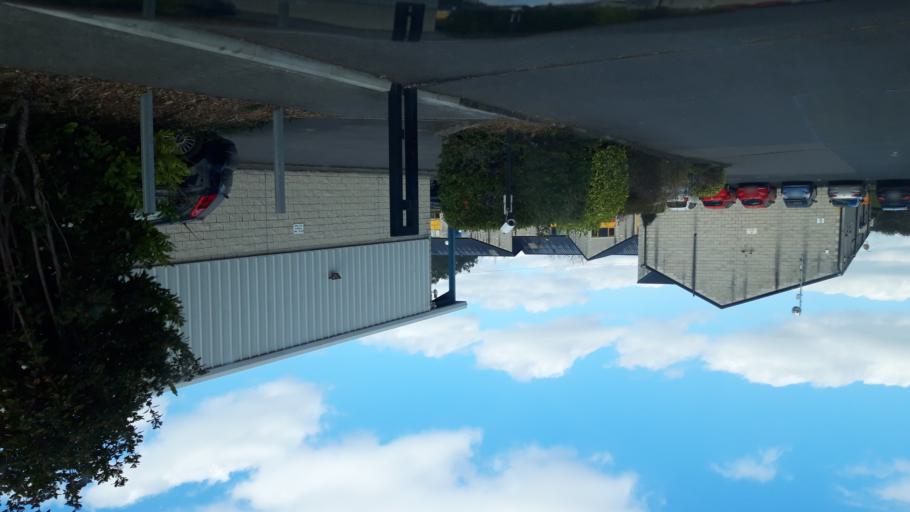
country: IE
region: Leinster
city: Donaghmede
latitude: 53.4260
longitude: -6.1719
